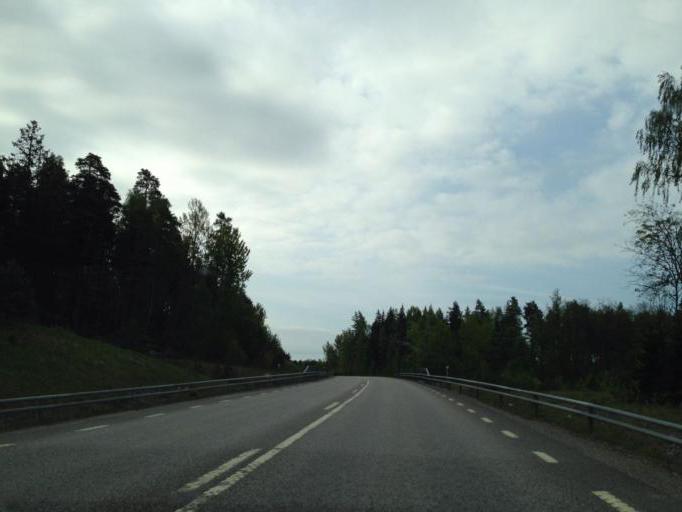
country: SE
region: Soedermanland
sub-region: Eskilstuna Kommun
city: Skogstorp
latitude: 59.3368
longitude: 16.4604
